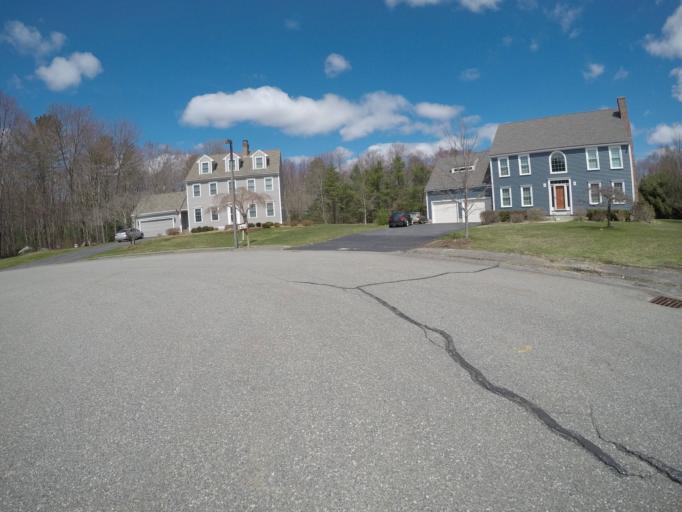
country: US
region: Massachusetts
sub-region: Bristol County
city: Easton
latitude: 42.0682
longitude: -71.1248
